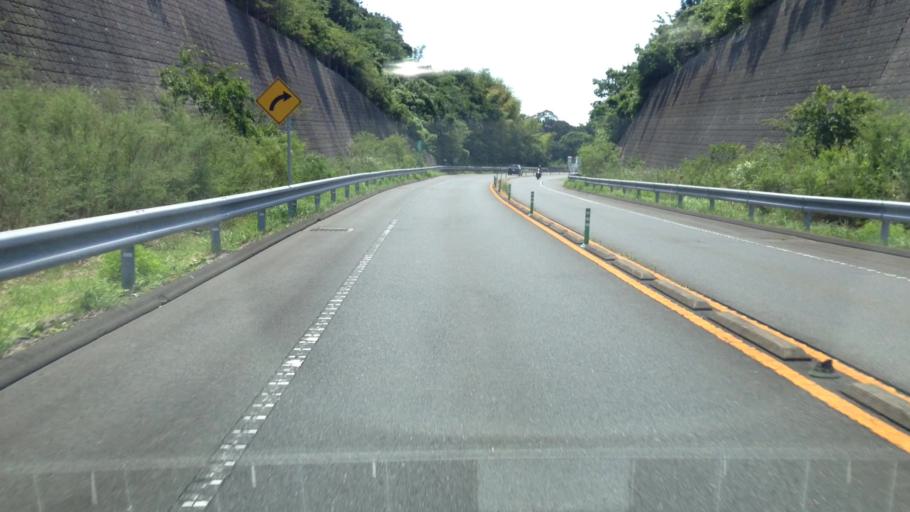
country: JP
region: Kanagawa
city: Yokosuka
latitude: 35.2344
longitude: 139.6504
